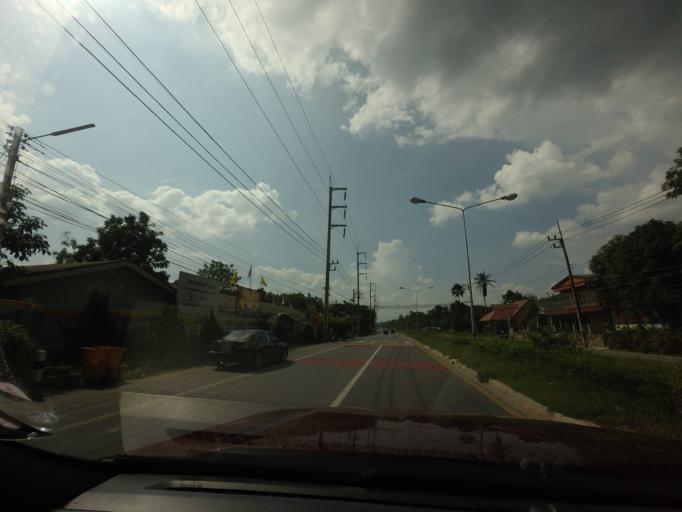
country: TH
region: Yala
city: Yala
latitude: 6.4805
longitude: 101.2655
